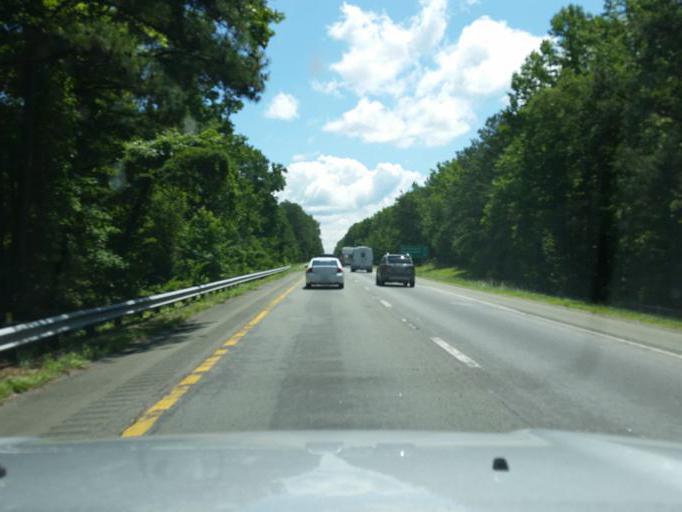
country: US
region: Virginia
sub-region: Henrico County
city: Sandston
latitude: 37.5137
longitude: -77.1728
